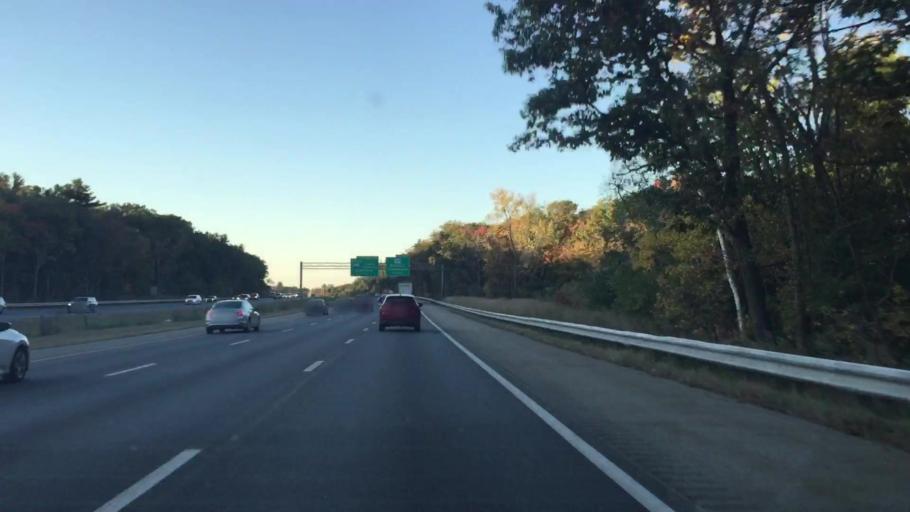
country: US
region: Massachusetts
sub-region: Middlesex County
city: Billerica
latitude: 42.5808
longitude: -71.3077
